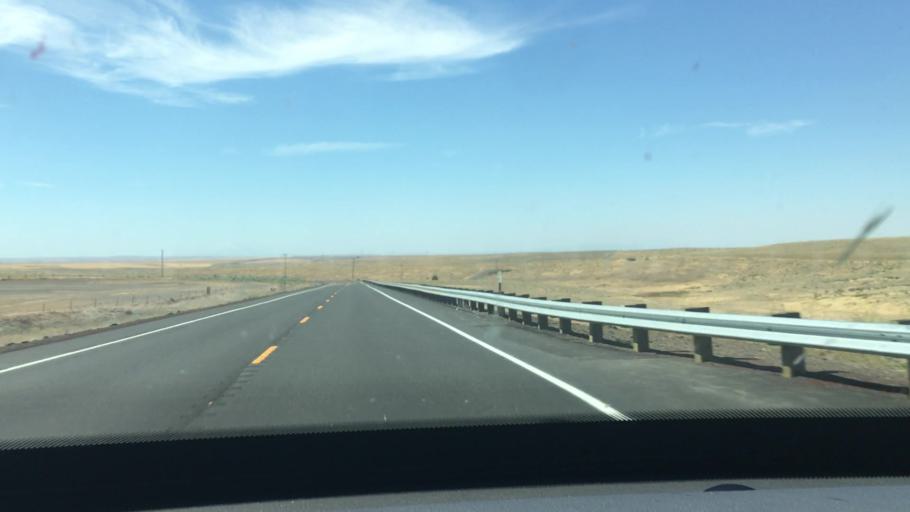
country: US
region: Oregon
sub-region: Sherman County
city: Moro
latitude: 45.2159
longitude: -120.7062
